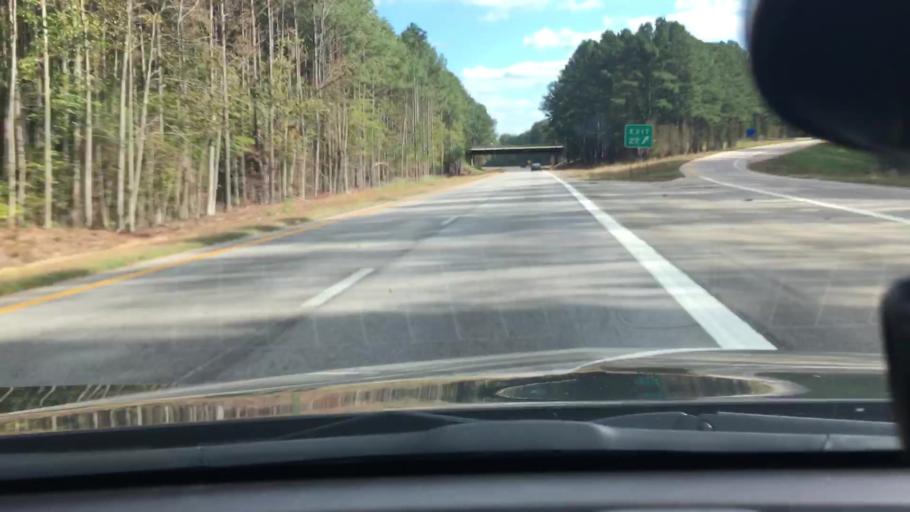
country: US
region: North Carolina
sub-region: Wake County
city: Zebulon
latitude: 35.8000
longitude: -78.1941
